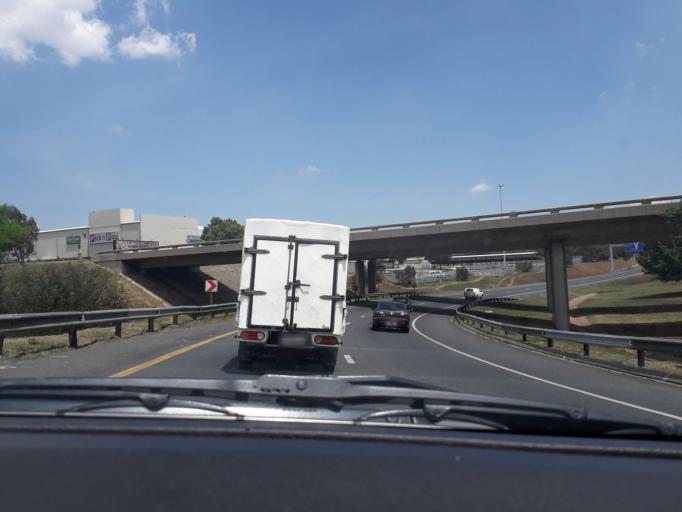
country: ZA
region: Gauteng
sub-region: City of Johannesburg Metropolitan Municipality
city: Johannesburg
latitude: -26.2638
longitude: 27.9855
